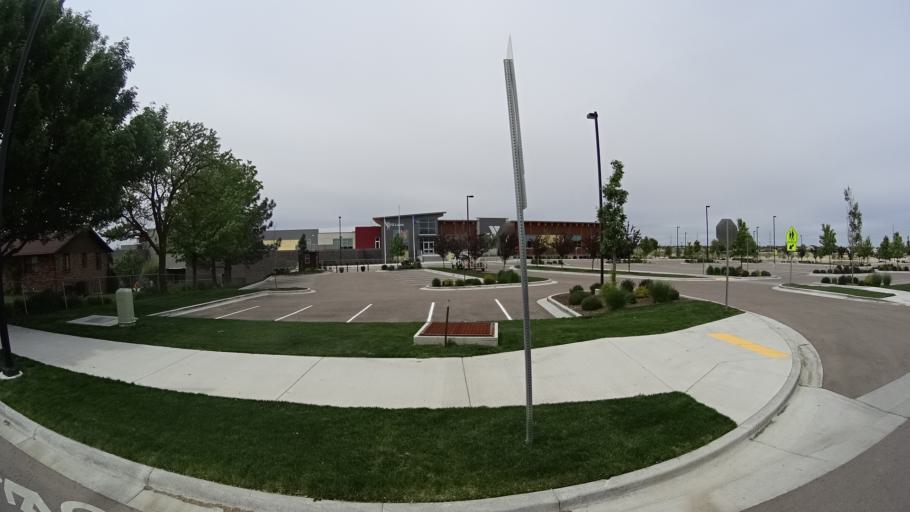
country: US
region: Idaho
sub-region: Ada County
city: Meridian
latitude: 43.5583
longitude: -116.3444
